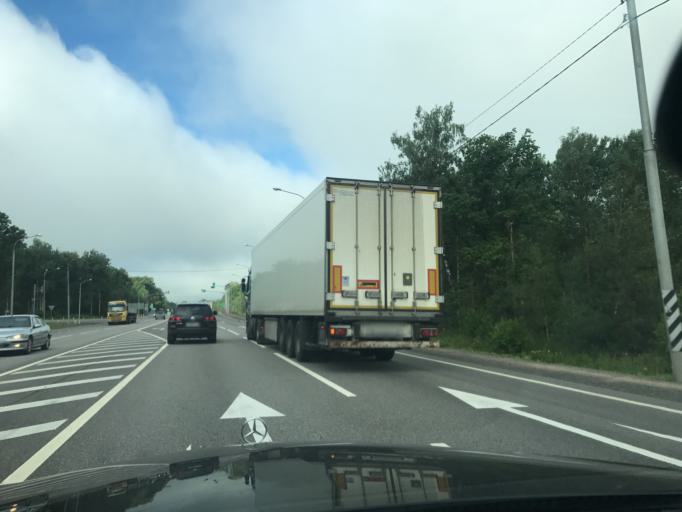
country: RU
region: Smolensk
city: Vyaz'ma
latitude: 55.2663
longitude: 34.3915
